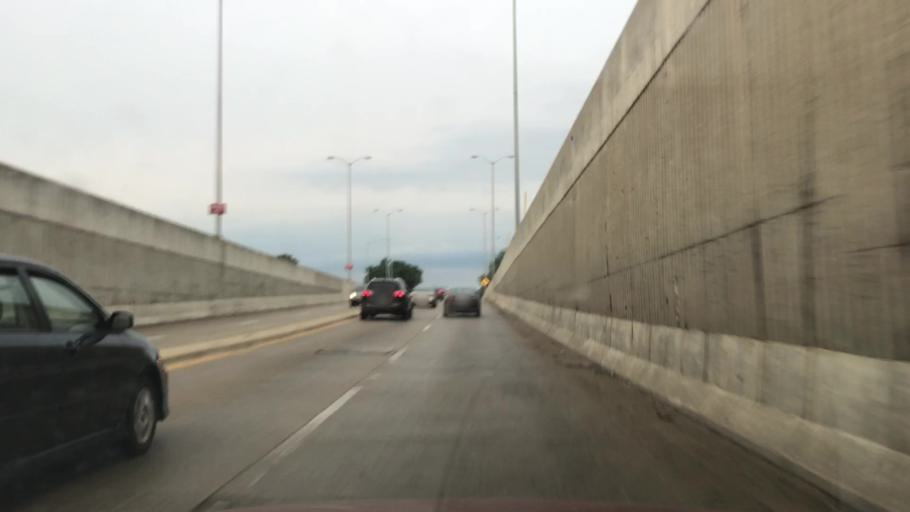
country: US
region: Illinois
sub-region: Cook County
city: Park Ridge
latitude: 42.0403
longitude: -87.8272
